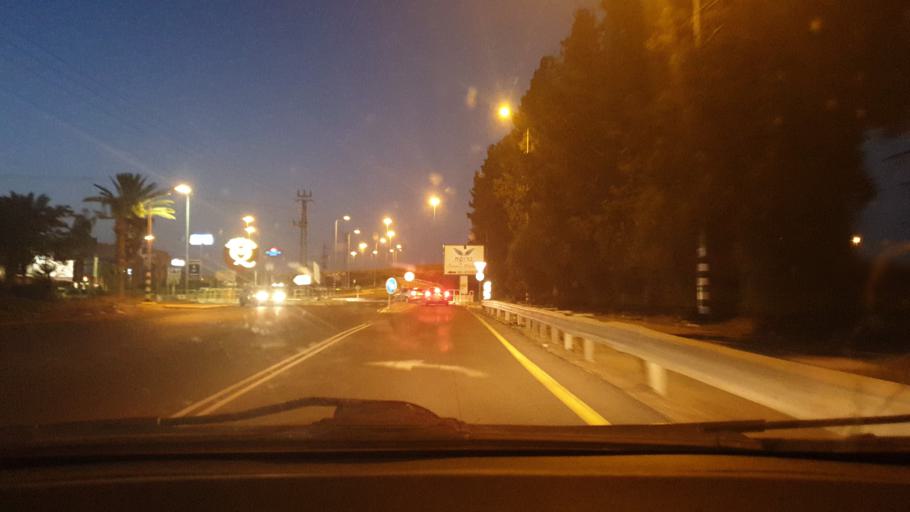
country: IL
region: Central District
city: Bene 'Ayish
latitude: 31.7989
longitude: 34.7618
